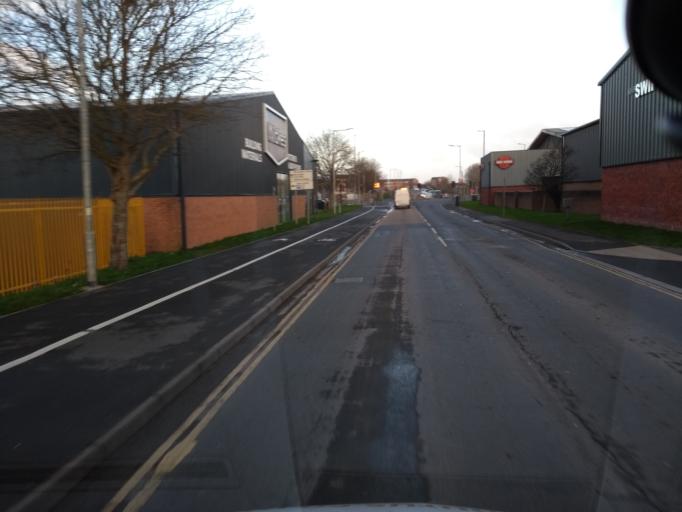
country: GB
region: England
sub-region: Somerset
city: Bridgwater
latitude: 51.1362
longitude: -2.9984
